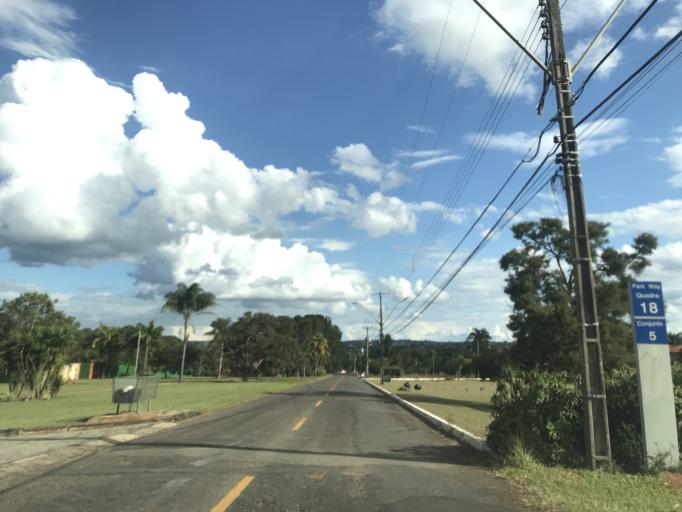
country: BR
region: Federal District
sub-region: Brasilia
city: Brasilia
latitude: -15.9119
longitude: -47.9414
